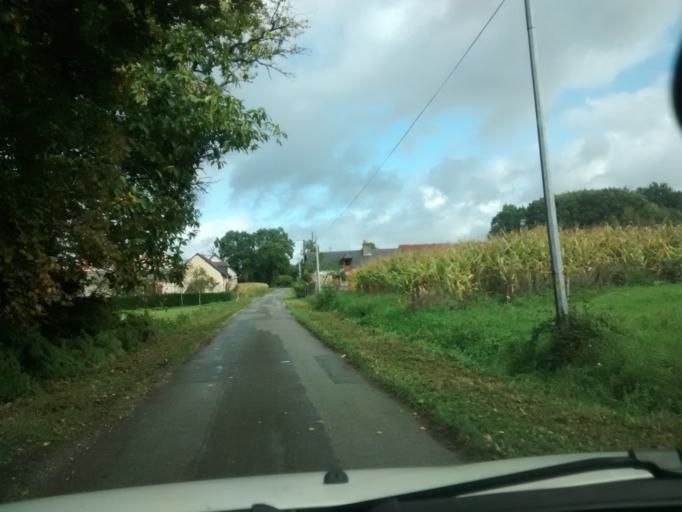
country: FR
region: Brittany
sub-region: Departement d'Ille-et-Vilaine
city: Chateaubourg
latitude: 48.1390
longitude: -1.4144
